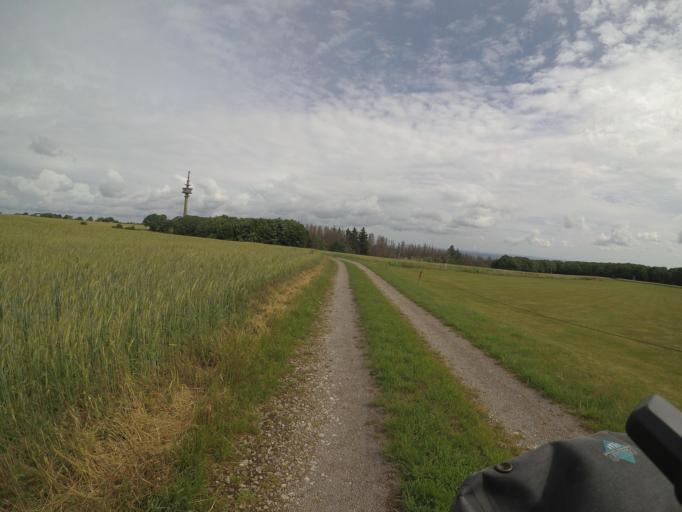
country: DE
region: North Rhine-Westphalia
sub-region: Regierungsbezirk Koln
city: Hurtgenwald
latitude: 50.7316
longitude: 6.4071
